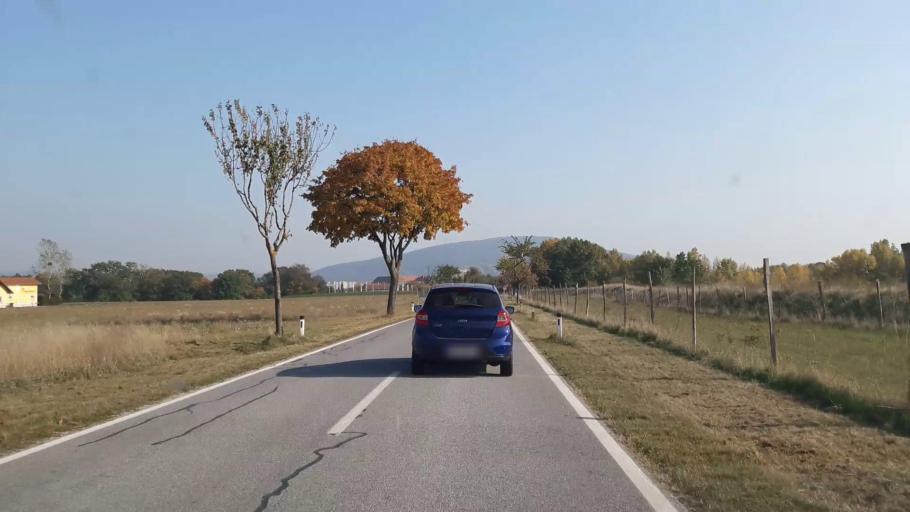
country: AT
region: Lower Austria
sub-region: Politischer Bezirk Ganserndorf
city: Marchegg
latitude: 48.2175
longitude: 16.9244
